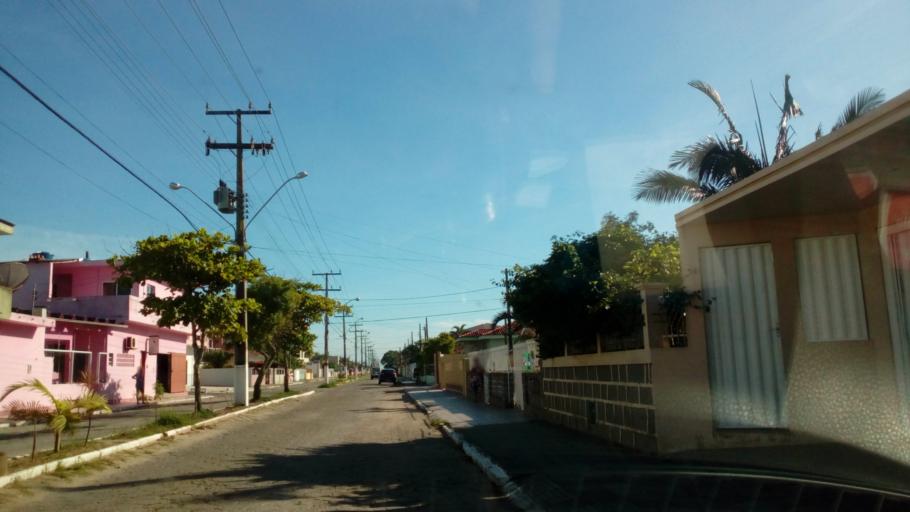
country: BR
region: Santa Catarina
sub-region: Laguna
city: Laguna
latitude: -28.4782
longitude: -48.7831
